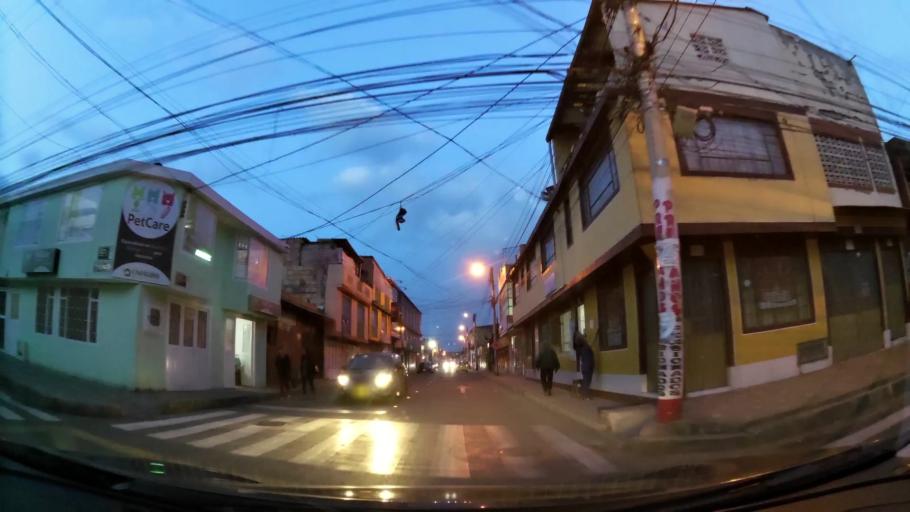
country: CO
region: Cundinamarca
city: Funza
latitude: 4.7167
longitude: -74.2138
